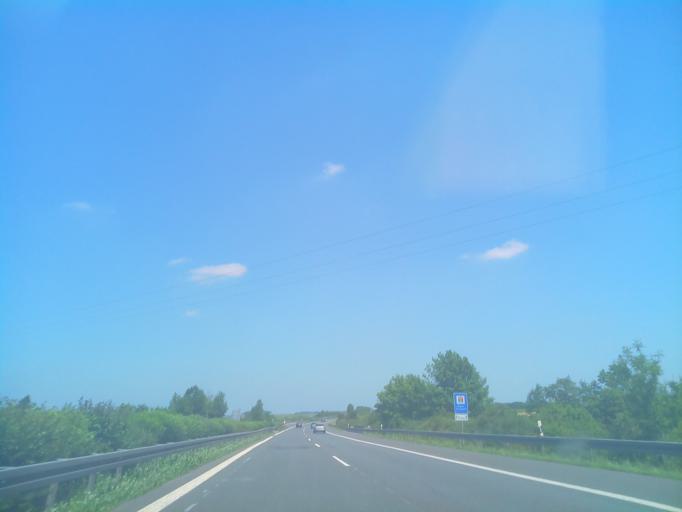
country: DE
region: Baden-Wuerttemberg
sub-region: Regierungsbezirk Stuttgart
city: Grunsfeld
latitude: 49.6297
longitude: 9.7297
